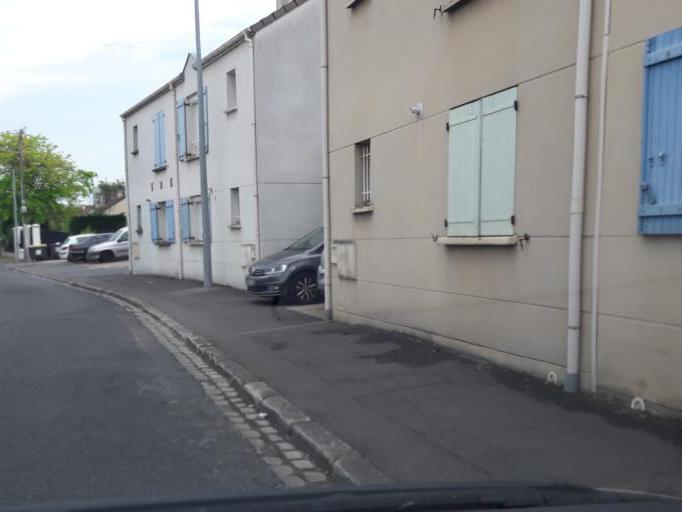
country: FR
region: Ile-de-France
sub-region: Departement de l'Essonne
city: Morsang-sur-Orge
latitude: 48.6604
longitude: 2.3540
